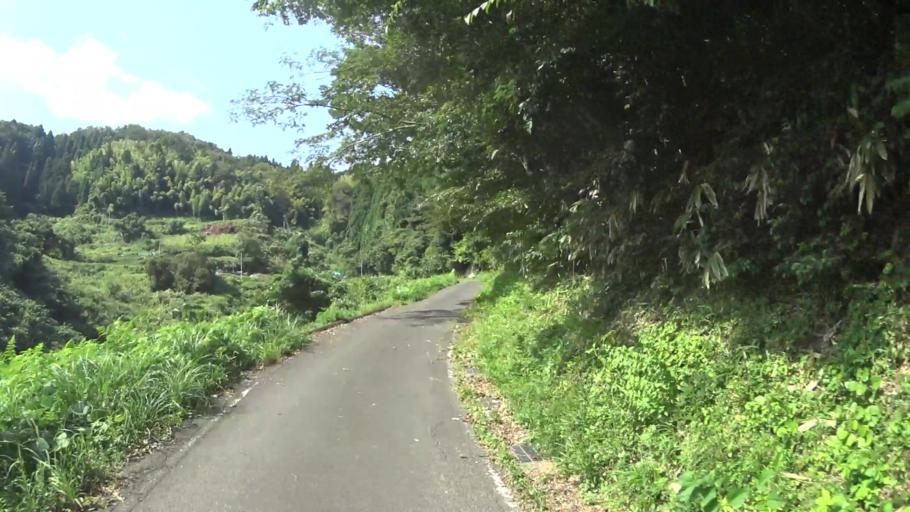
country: JP
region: Kyoto
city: Miyazu
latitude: 35.6566
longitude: 135.2440
